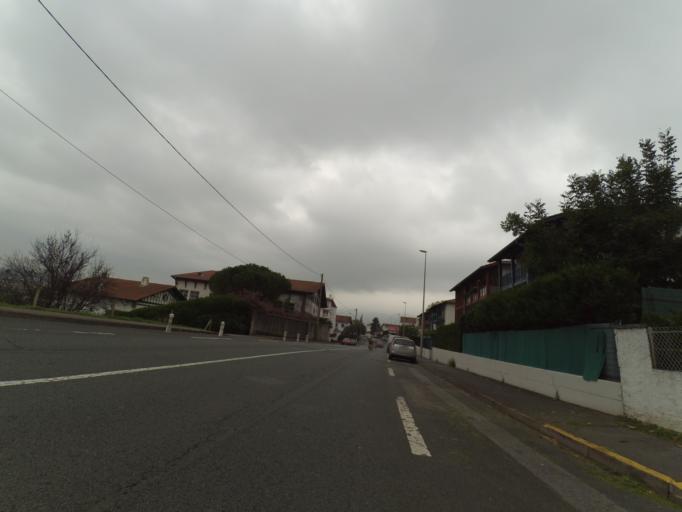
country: ES
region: Basque Country
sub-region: Provincia de Guipuzcoa
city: Irun
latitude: 43.3497
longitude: -1.7780
